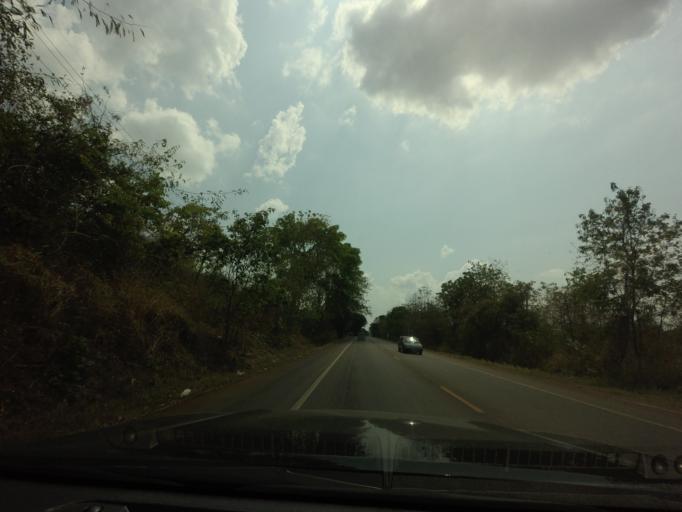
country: TH
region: Kanchanaburi
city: Sai Yok
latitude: 14.1512
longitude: 99.1426
